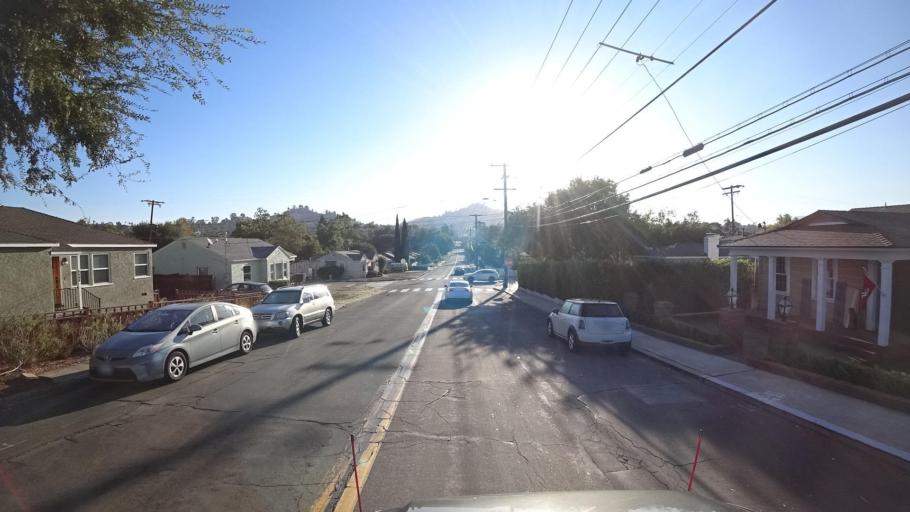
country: US
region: California
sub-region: San Diego County
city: La Mesa
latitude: 32.7683
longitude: -117.0063
